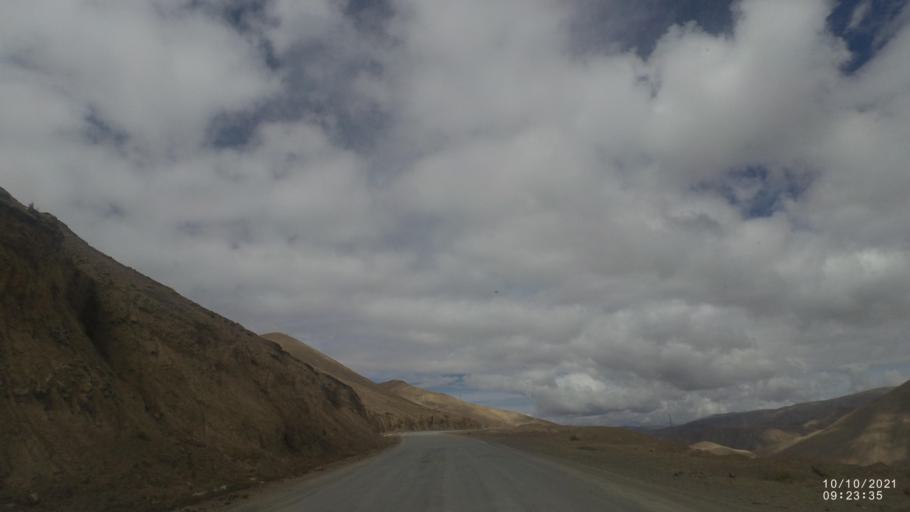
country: BO
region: La Paz
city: Quime
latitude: -17.0858
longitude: -67.3040
